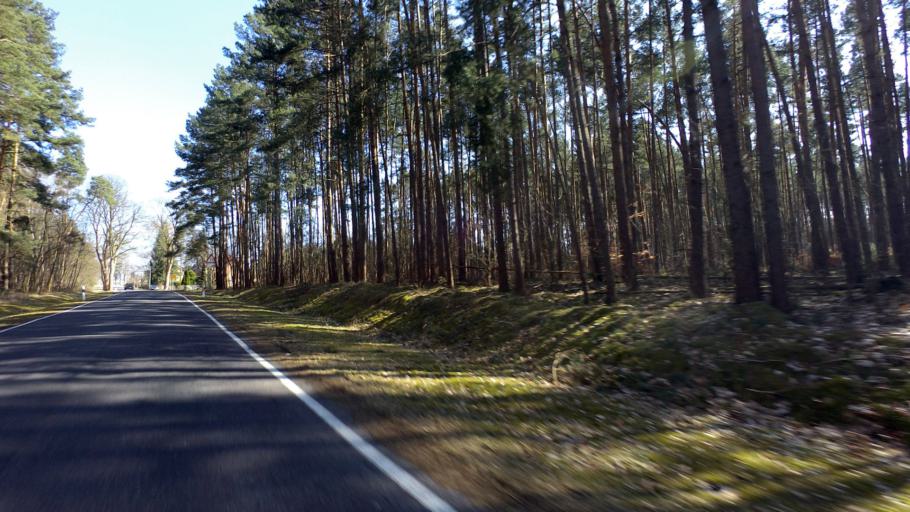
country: DE
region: Brandenburg
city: Wiesenburg
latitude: 52.0785
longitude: 12.5126
